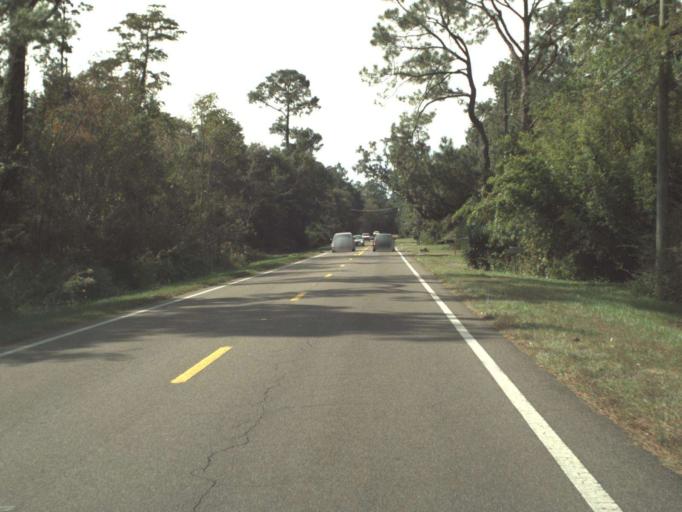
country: US
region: Florida
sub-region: Escambia County
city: Myrtle Grove
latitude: 30.4183
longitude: -87.3557
